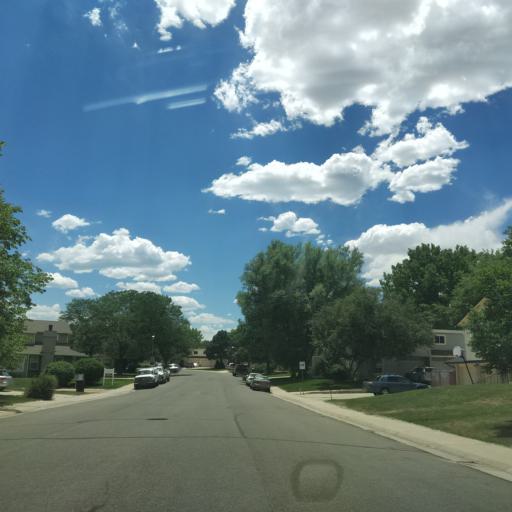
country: US
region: Colorado
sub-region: Jefferson County
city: Lakewood
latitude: 39.6860
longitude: -105.1128
